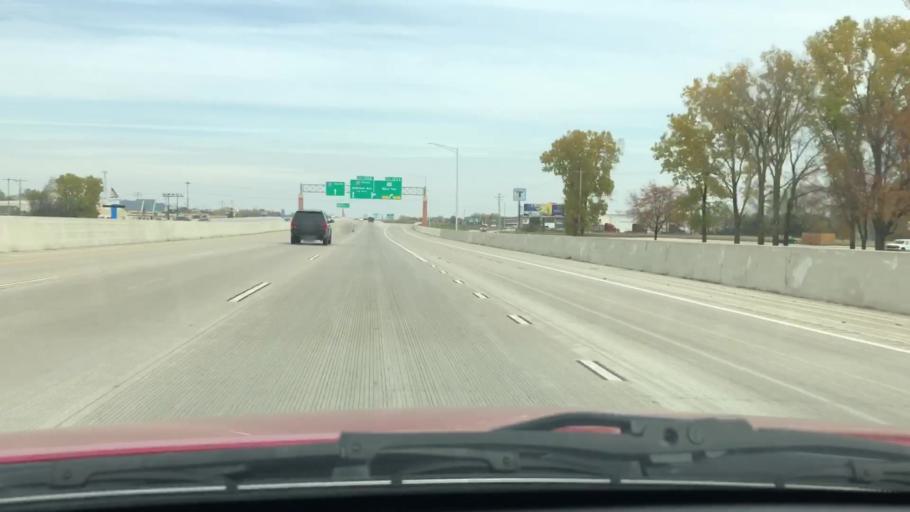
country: US
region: Wisconsin
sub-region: Brown County
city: De Pere
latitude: 44.4471
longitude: -88.0935
